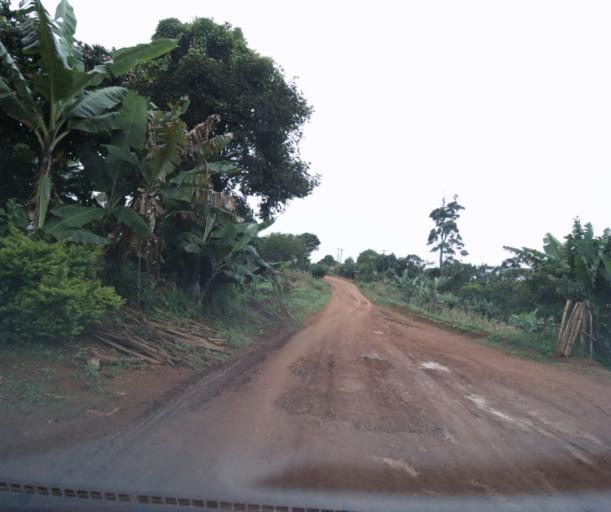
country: CM
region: West
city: Dschang
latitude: 5.5114
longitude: 9.9824
